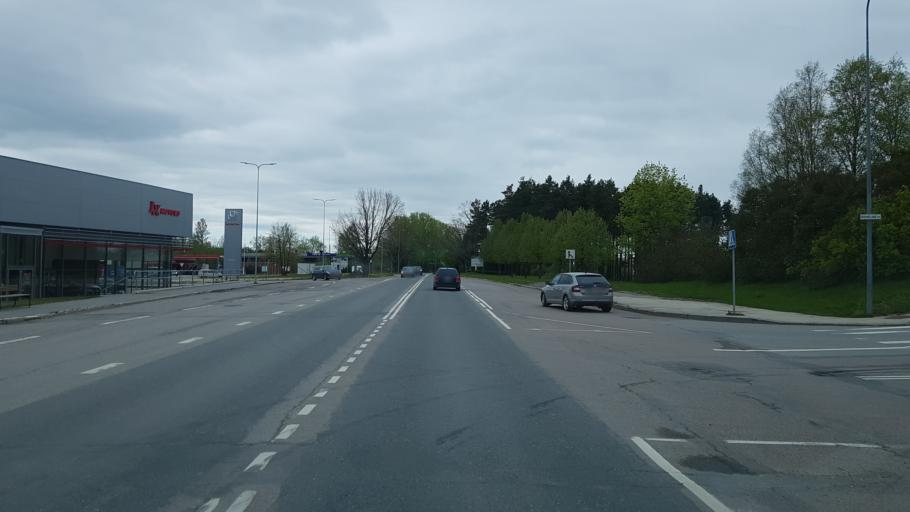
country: EE
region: Viljandimaa
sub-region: Viljandi linn
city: Viljandi
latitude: 58.3771
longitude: 25.5971
